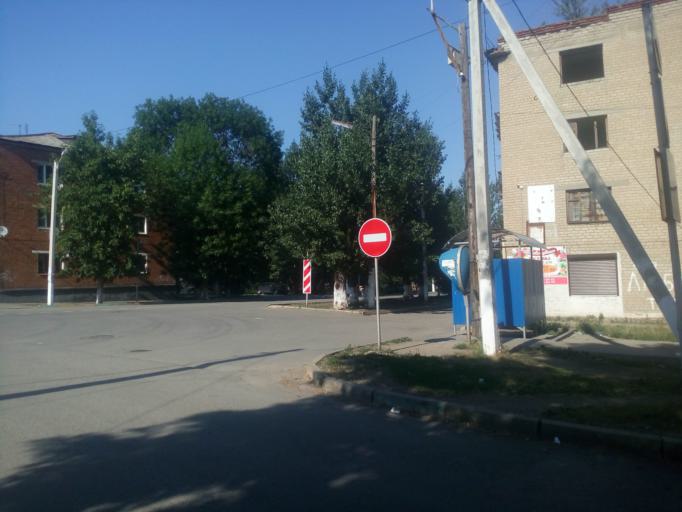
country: RU
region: Rostov
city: Sholokhovskiy
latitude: 48.2816
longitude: 41.0547
